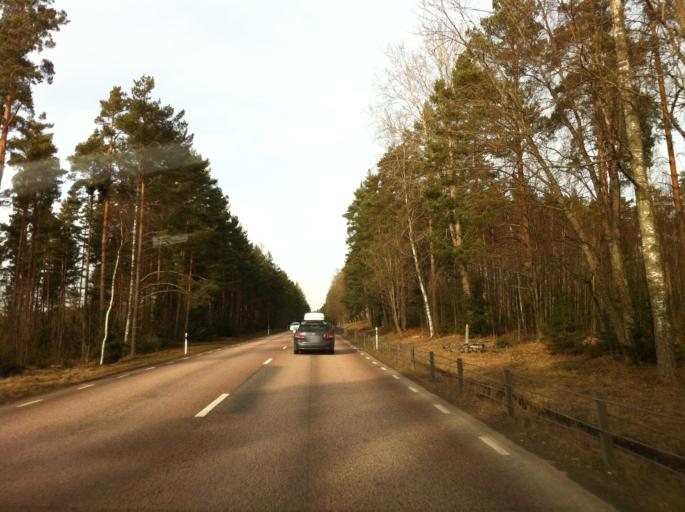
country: SE
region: Vaestra Goetaland
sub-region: Gullspangs Kommun
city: Gullspang
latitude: 59.0669
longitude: 14.1532
